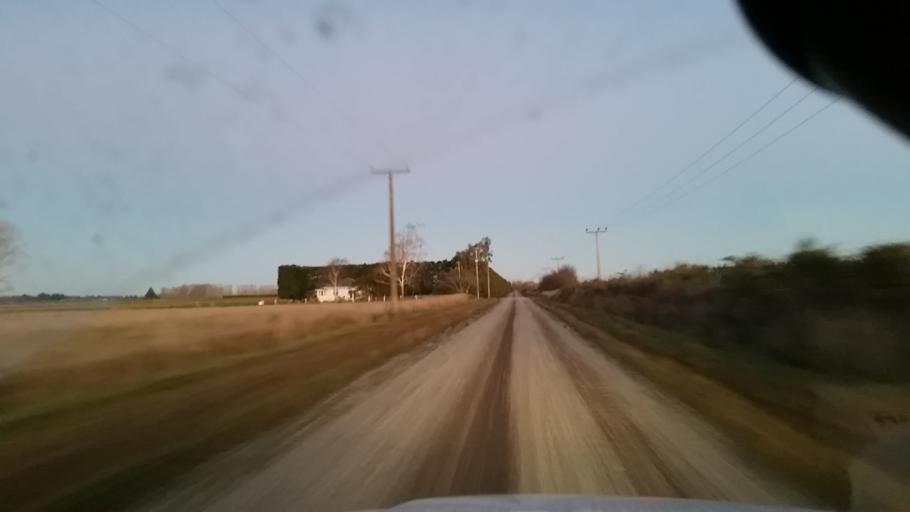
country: NZ
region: Canterbury
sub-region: Ashburton District
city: Tinwald
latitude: -43.9965
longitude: 171.6629
